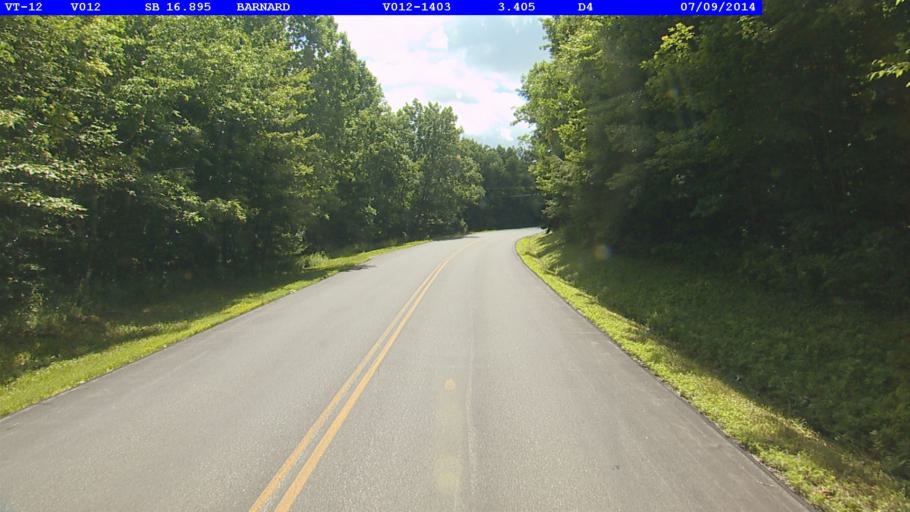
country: US
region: Vermont
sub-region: Windsor County
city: Woodstock
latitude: 43.7105
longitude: -72.6207
